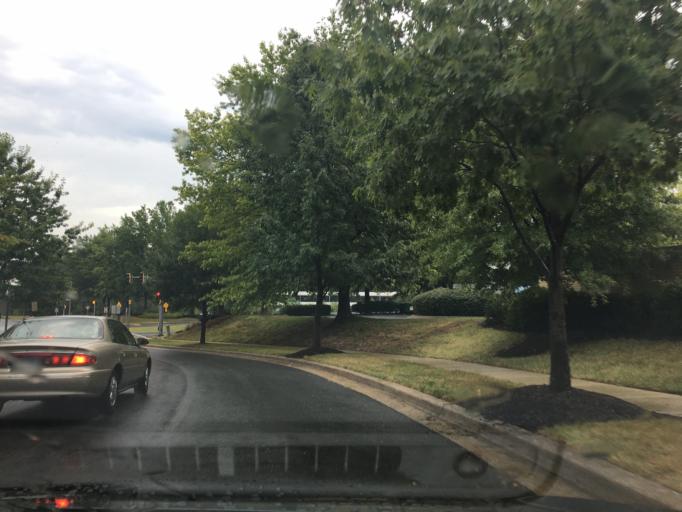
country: US
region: Maryland
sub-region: Montgomery County
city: Gaithersburg
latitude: 39.1298
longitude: -77.2304
